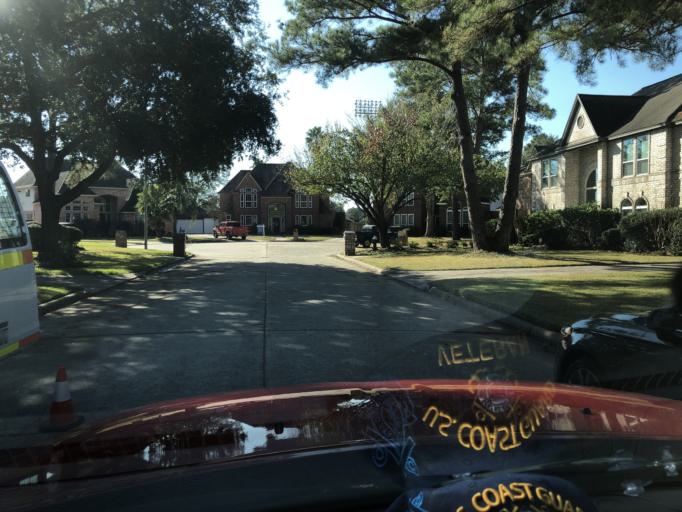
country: US
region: Texas
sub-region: Harris County
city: Tomball
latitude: 30.0328
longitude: -95.5480
